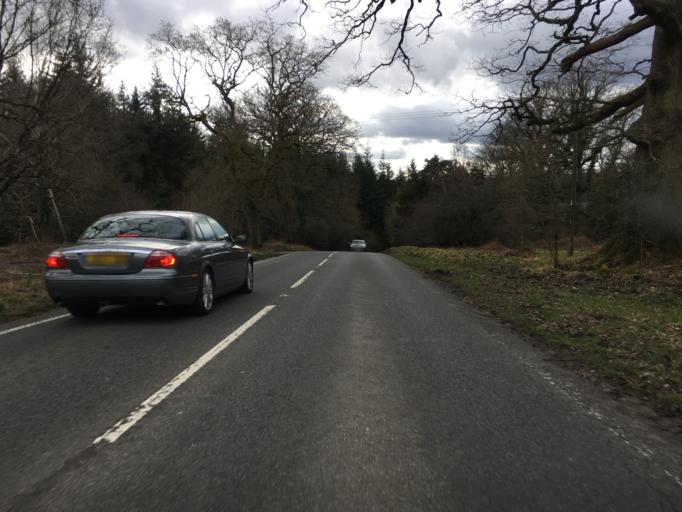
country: GB
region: England
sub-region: Gloucestershire
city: Lydbrook
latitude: 51.8048
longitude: -2.5564
